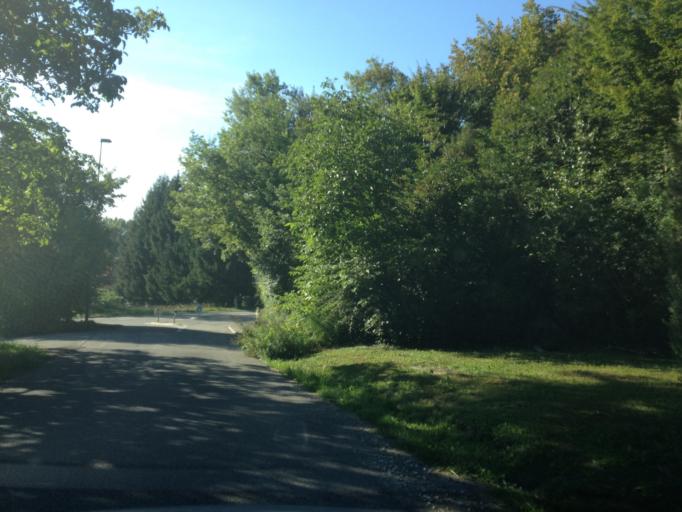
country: FR
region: Rhone-Alpes
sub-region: Departement de la Savoie
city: Mery
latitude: 45.6550
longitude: 5.9392
